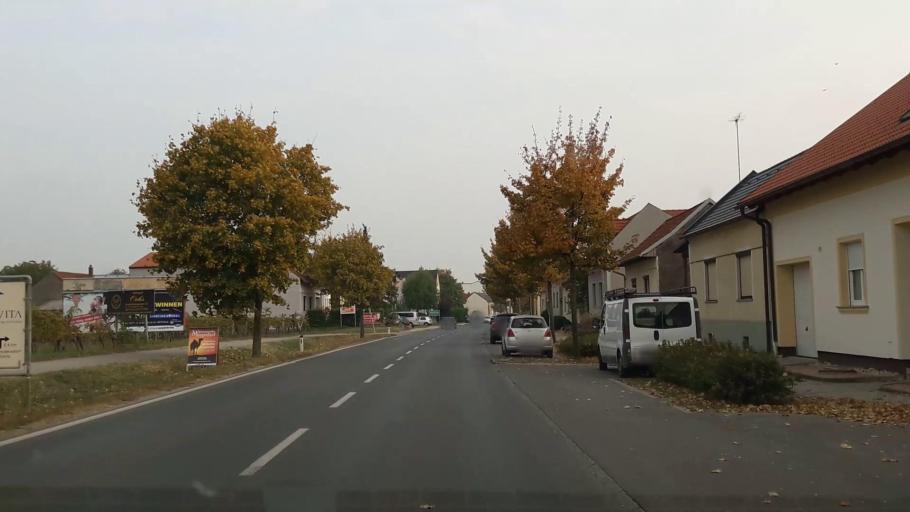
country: AT
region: Burgenland
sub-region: Politischer Bezirk Neusiedl am See
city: Weiden am See
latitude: 47.9332
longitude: 16.8609
